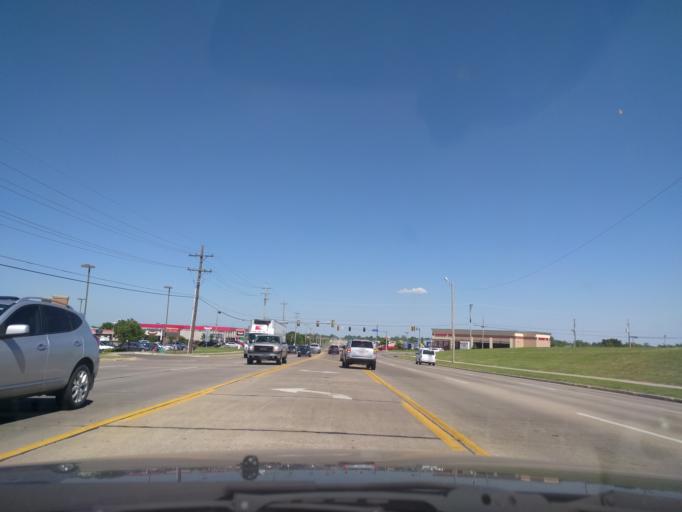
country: US
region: Oklahoma
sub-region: Tulsa County
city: Broken Arrow
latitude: 36.0610
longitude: -95.7826
